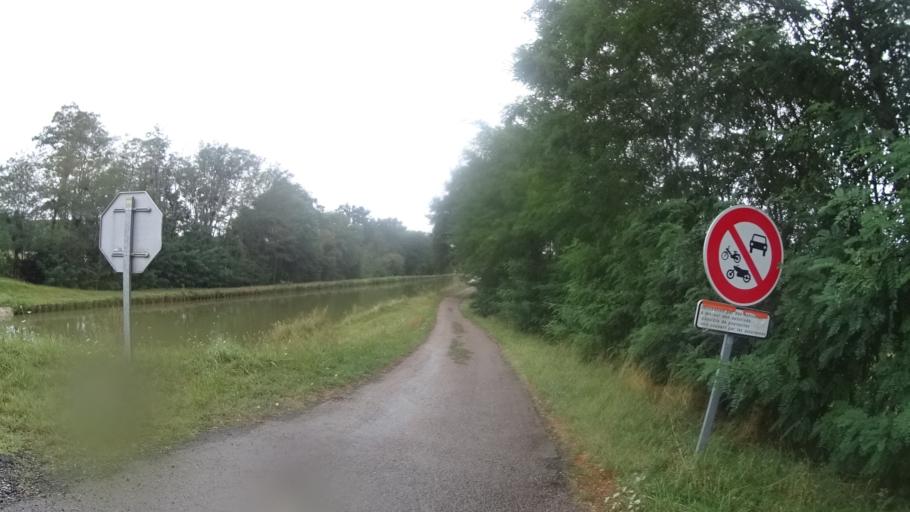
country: FR
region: Bourgogne
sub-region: Departement de la Nievre
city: Saint-Leger-des-Vignes
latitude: 46.8125
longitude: 3.3695
